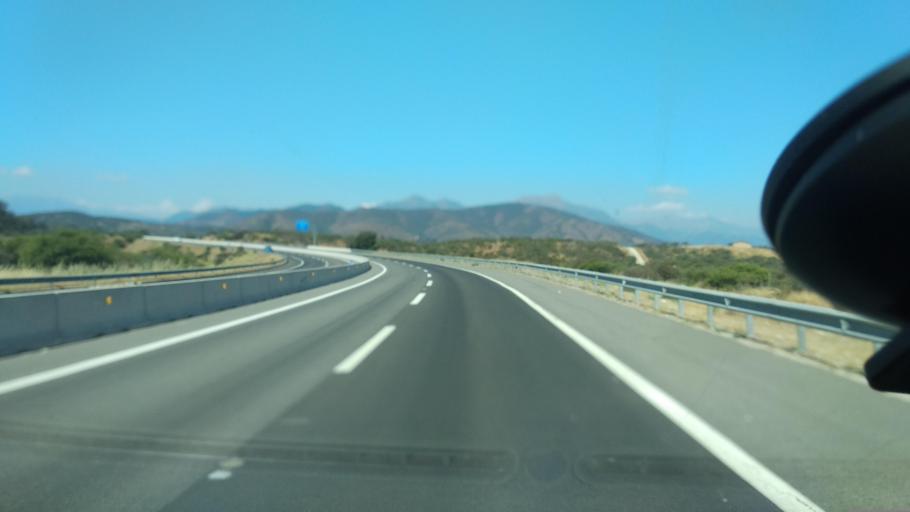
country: CL
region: Valparaiso
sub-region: Provincia de Marga Marga
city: Limache
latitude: -32.9867
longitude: -71.3214
